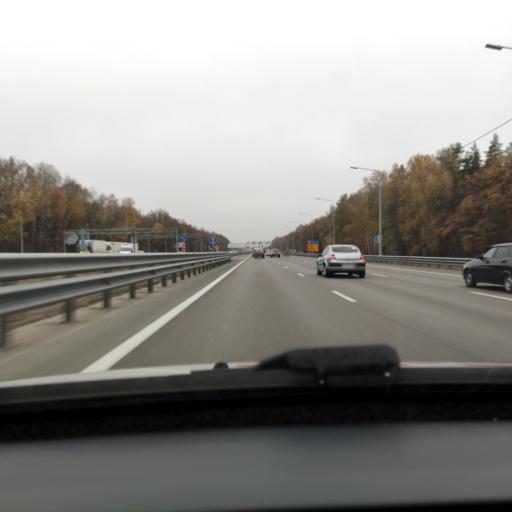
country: RU
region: Voronezj
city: Podgornoye
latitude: 51.7644
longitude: 39.1902
